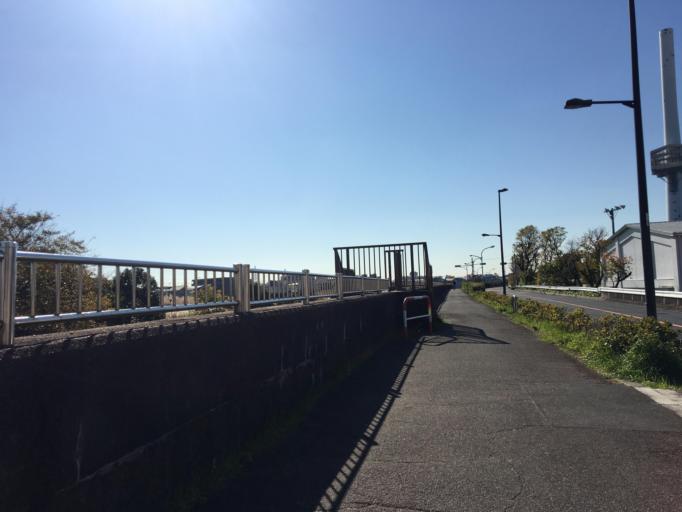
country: JP
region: Tokyo
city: Urayasu
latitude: 35.6866
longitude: 139.9084
